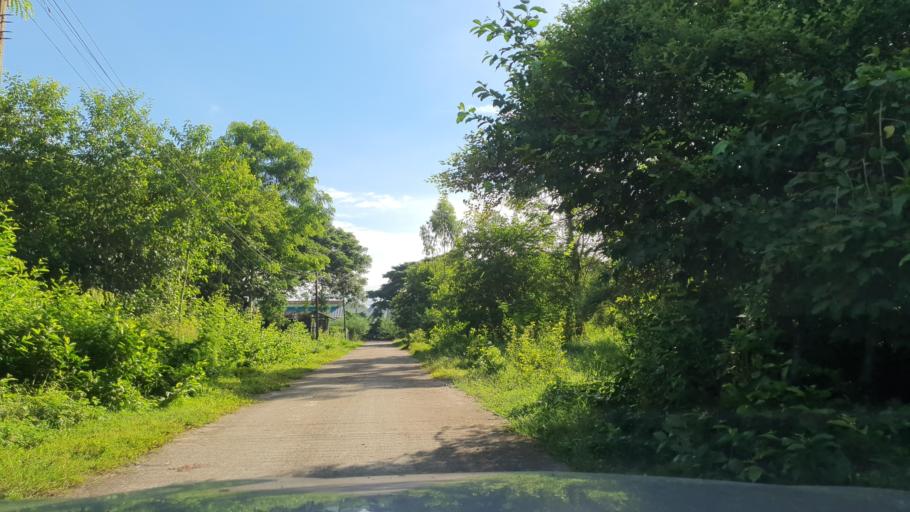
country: TH
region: Chiang Mai
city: San Kamphaeng
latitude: 18.7487
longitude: 99.1039
